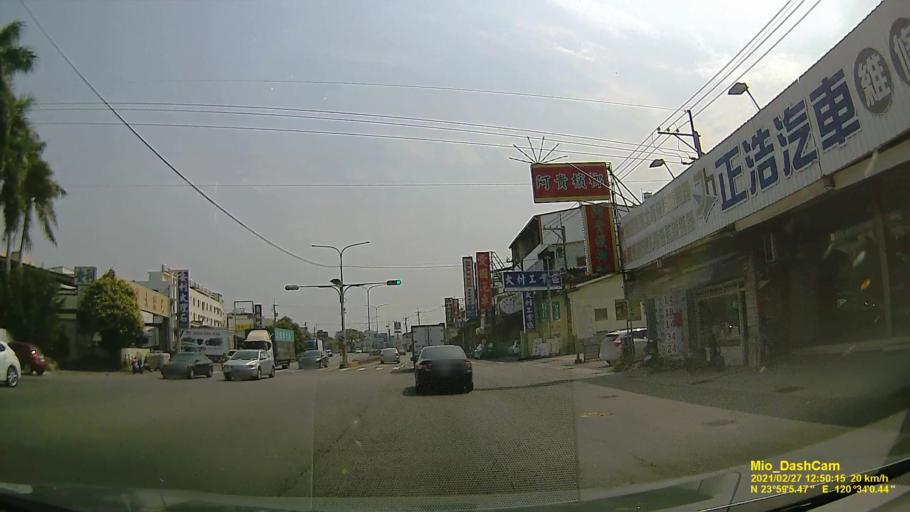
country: TW
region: Taiwan
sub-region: Changhua
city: Chang-hua
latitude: 23.9848
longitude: 120.5668
